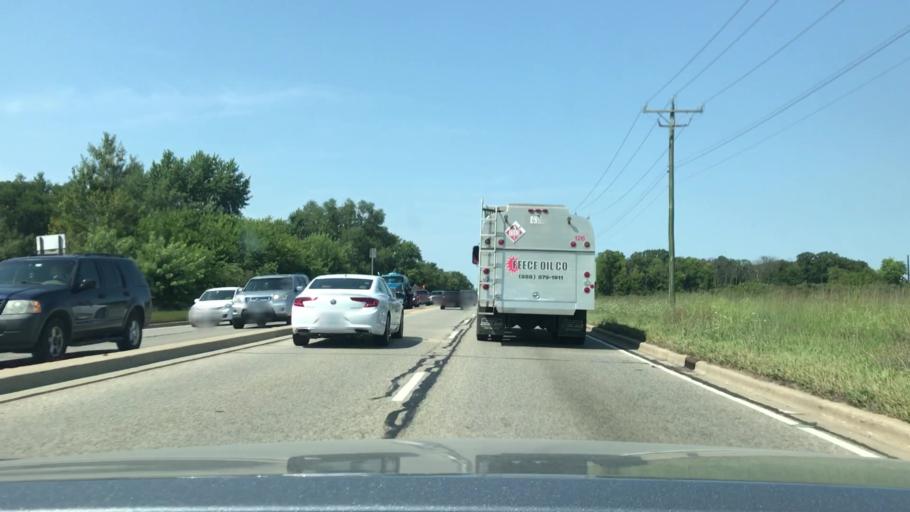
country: US
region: Illinois
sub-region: Kane County
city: Batavia
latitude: 41.8371
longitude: -88.2794
